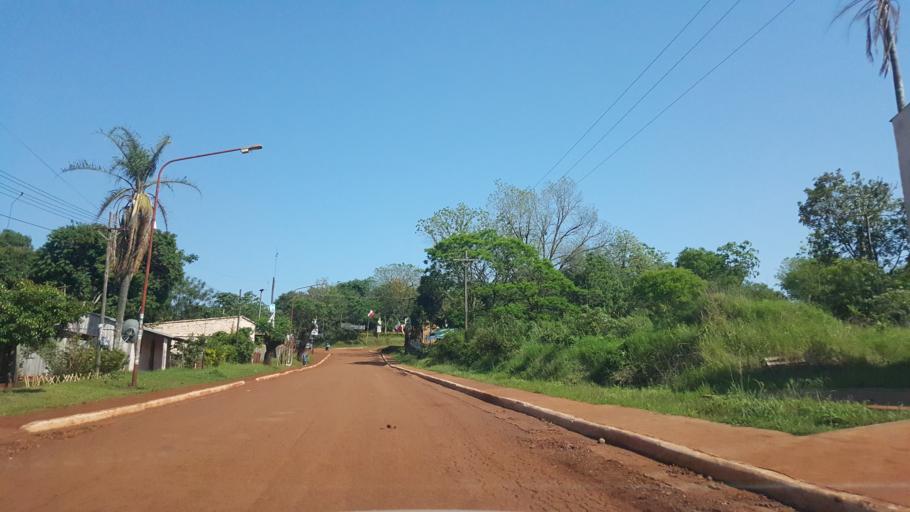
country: AR
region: Corrientes
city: San Carlos
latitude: -27.7453
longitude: -55.8942
